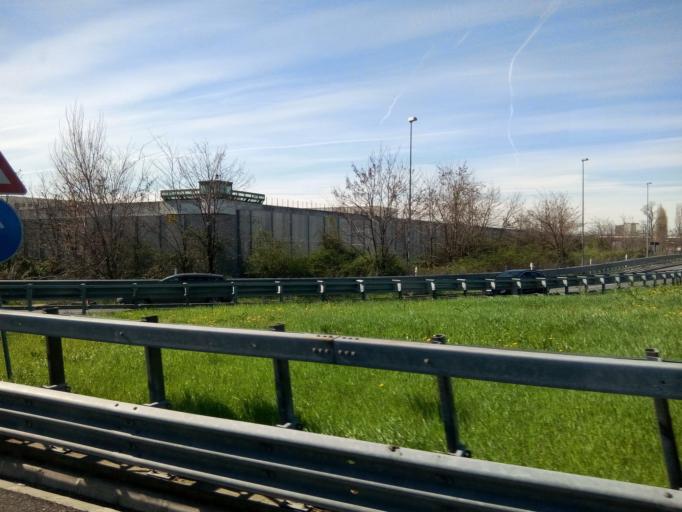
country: IT
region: Lombardy
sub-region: Citta metropolitana di Milano
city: Pero
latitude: 45.5286
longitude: 9.0963
